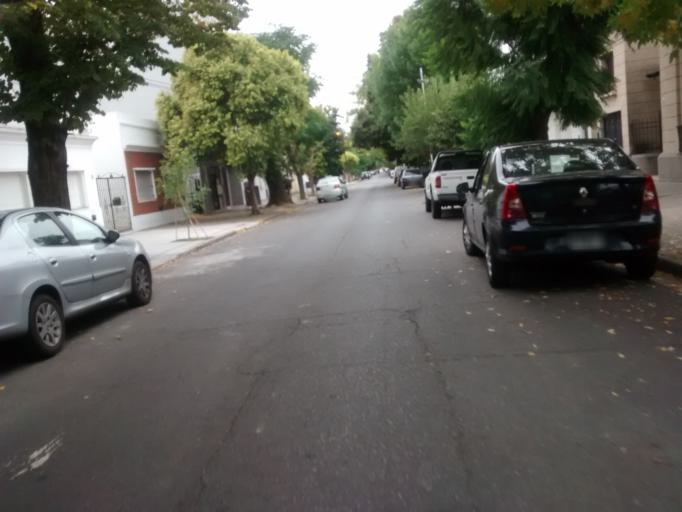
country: AR
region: Buenos Aires
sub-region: Partido de La Plata
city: La Plata
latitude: -34.9385
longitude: -57.9423
